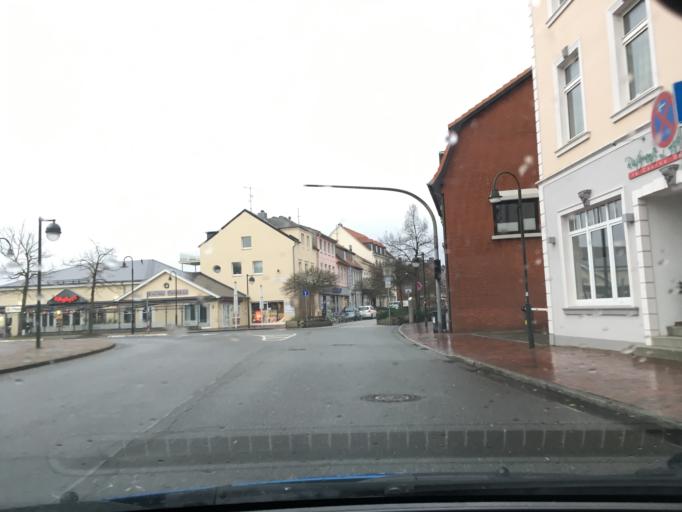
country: DE
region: Schleswig-Holstein
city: Molln
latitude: 53.6265
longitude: 10.6851
